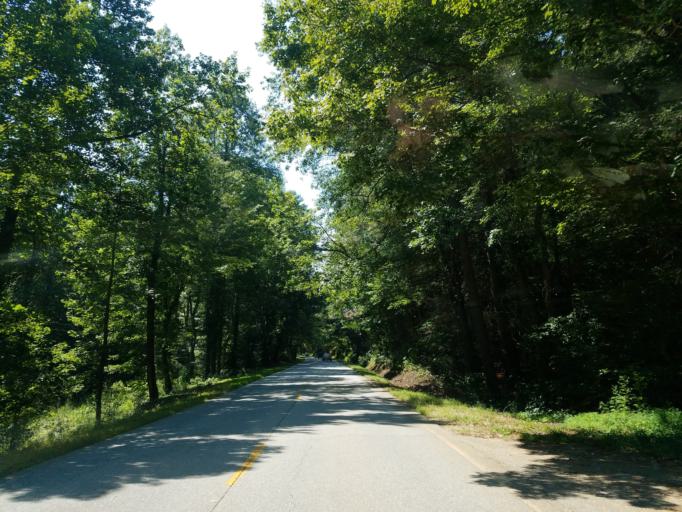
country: US
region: Georgia
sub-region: Lumpkin County
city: Dahlonega
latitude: 34.6344
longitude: -83.9290
